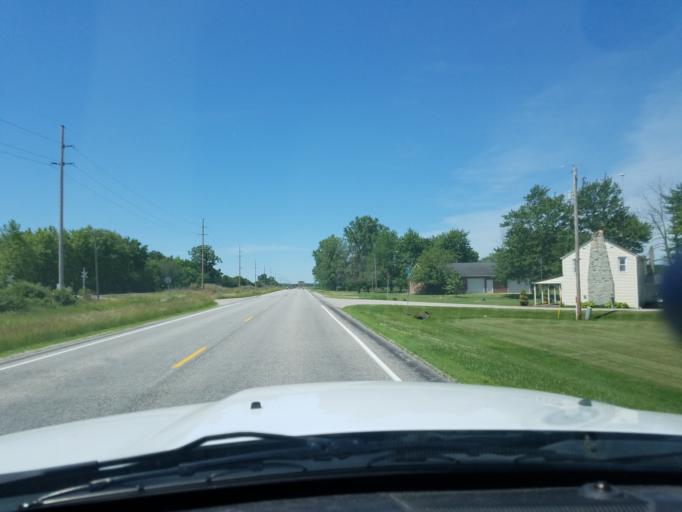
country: US
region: Indiana
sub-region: Jay County
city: Portland
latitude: 40.4038
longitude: -85.0564
